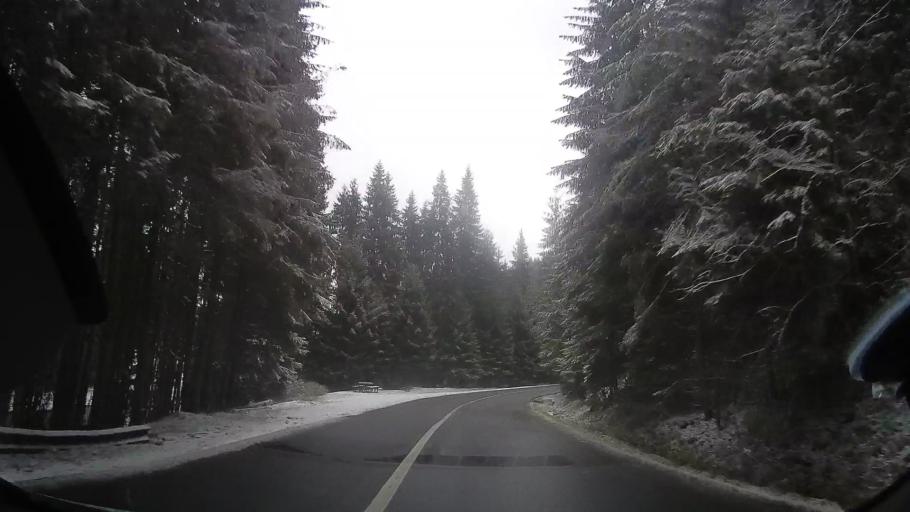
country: RO
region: Cluj
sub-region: Comuna Belis
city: Belis
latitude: 46.6559
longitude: 23.0537
